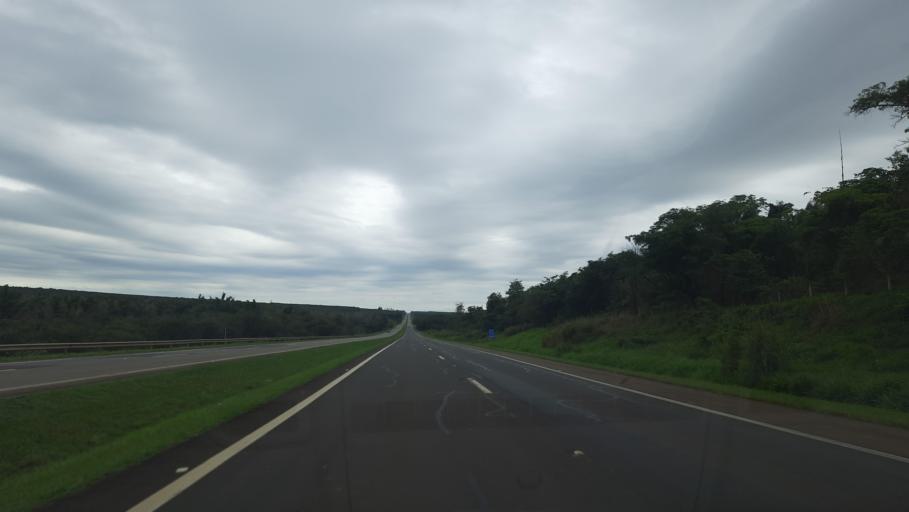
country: BR
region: Sao Paulo
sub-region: Casa Branca
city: Casa Branca
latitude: -21.8396
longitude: -47.0663
